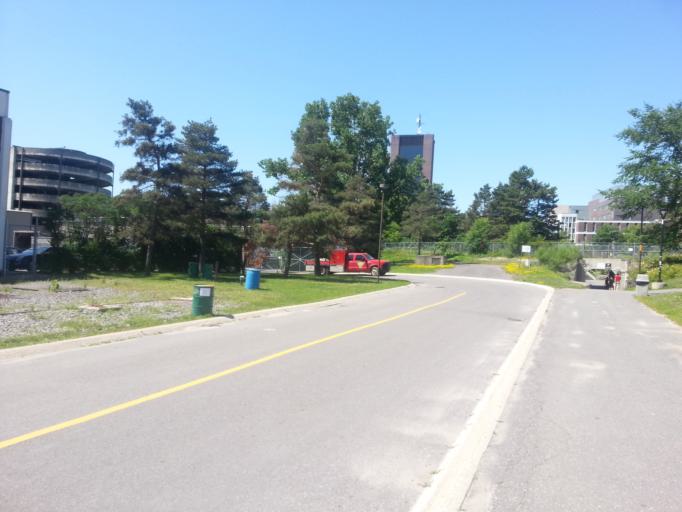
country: CA
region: Ontario
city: Ottawa
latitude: 45.3851
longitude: -75.6950
